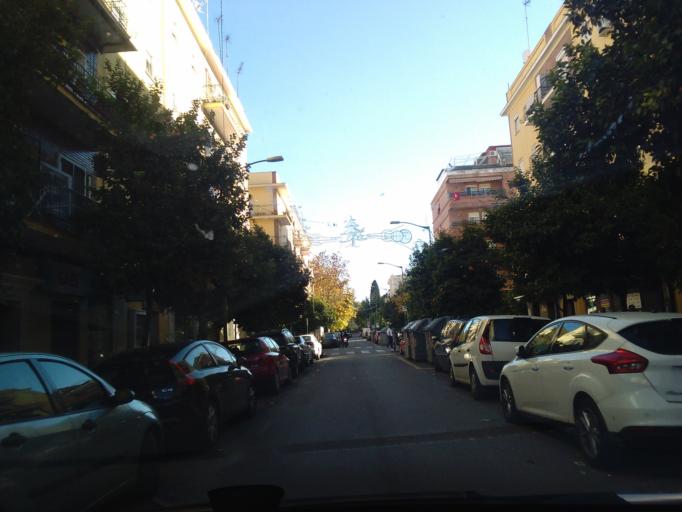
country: ES
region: Andalusia
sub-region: Provincia de Sevilla
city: Sevilla
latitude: 37.3606
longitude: -5.9791
